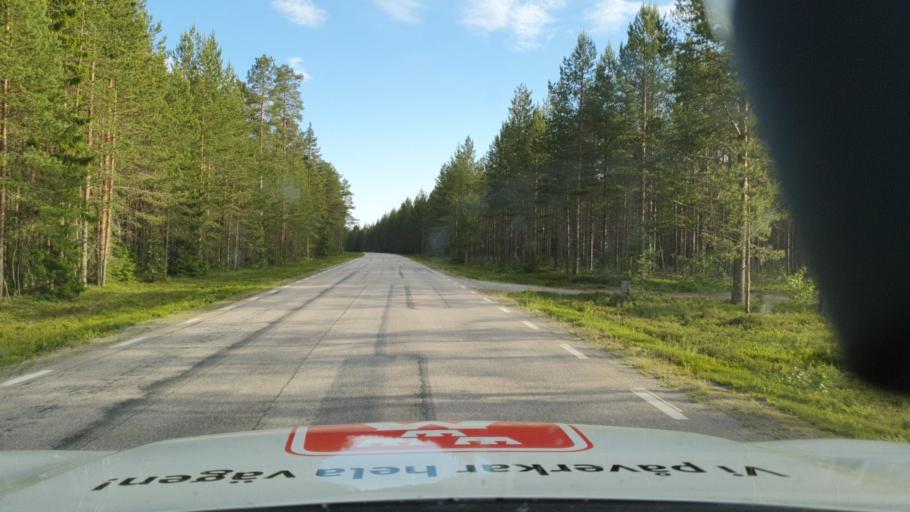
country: SE
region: Vaesterbotten
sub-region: Umea Kommun
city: Roback
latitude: 63.8677
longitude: 20.1461
